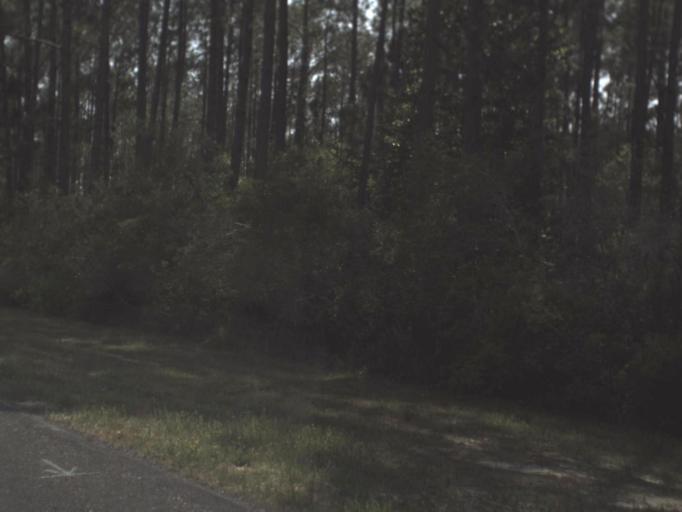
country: US
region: Florida
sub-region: Santa Rosa County
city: Bagdad
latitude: 30.4981
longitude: -87.0807
